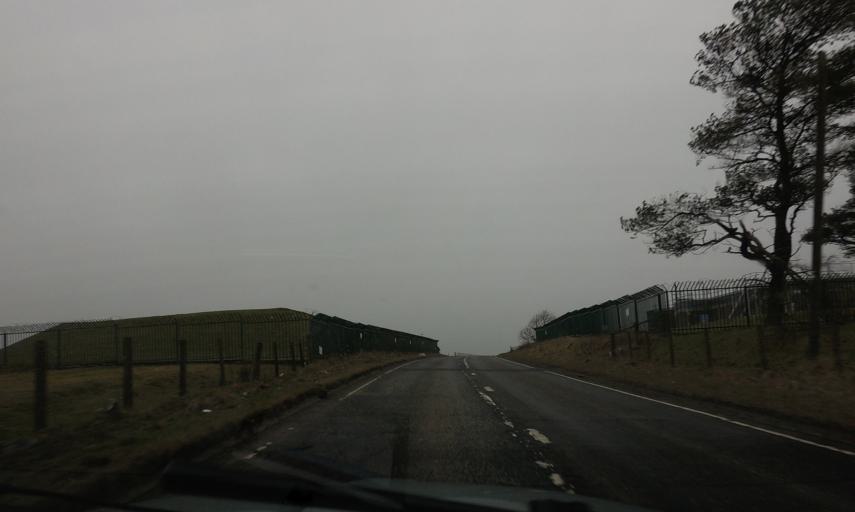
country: GB
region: Scotland
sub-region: North Lanarkshire
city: Shotts
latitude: 55.8494
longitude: -3.8172
